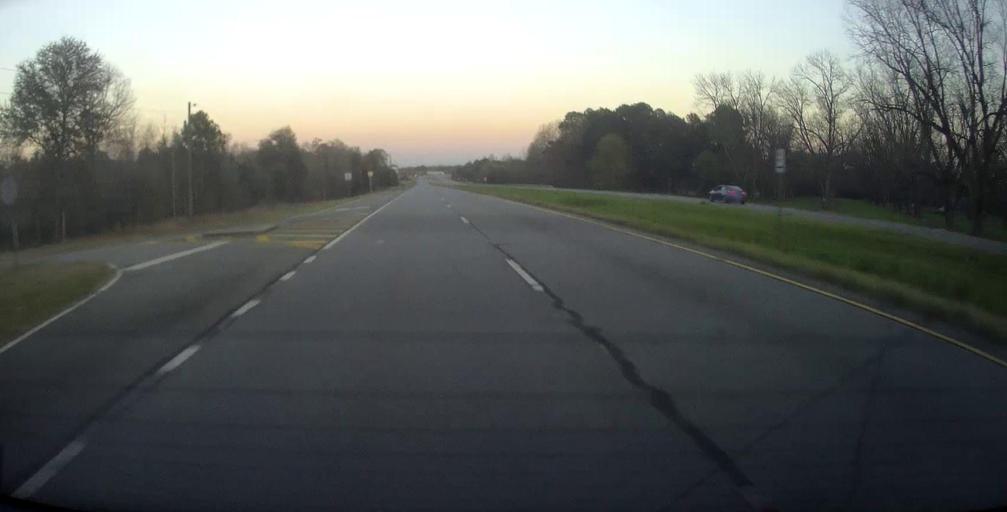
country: US
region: Georgia
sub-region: Dodge County
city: Eastman
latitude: 32.1768
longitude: -83.1737
